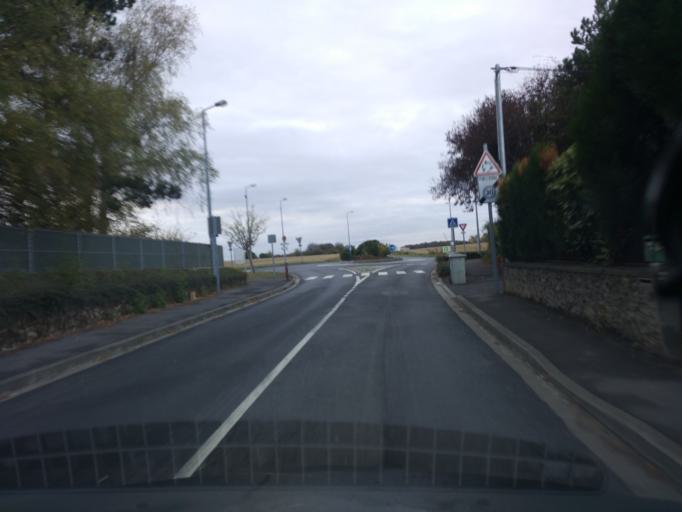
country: FR
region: Ile-de-France
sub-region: Departement de l'Essonne
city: Les Molieres
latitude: 48.6702
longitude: 2.0658
